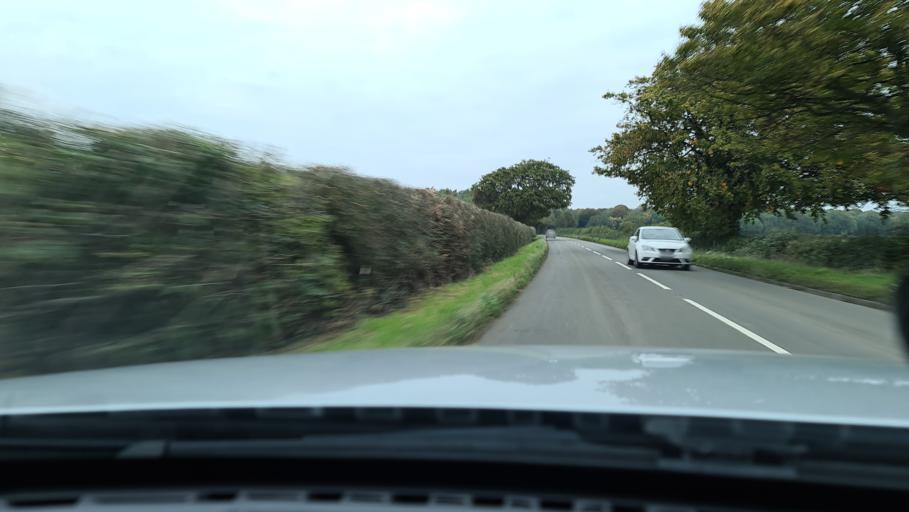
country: GB
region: England
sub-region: Oxfordshire
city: Somerton
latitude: 51.9211
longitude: -1.2402
